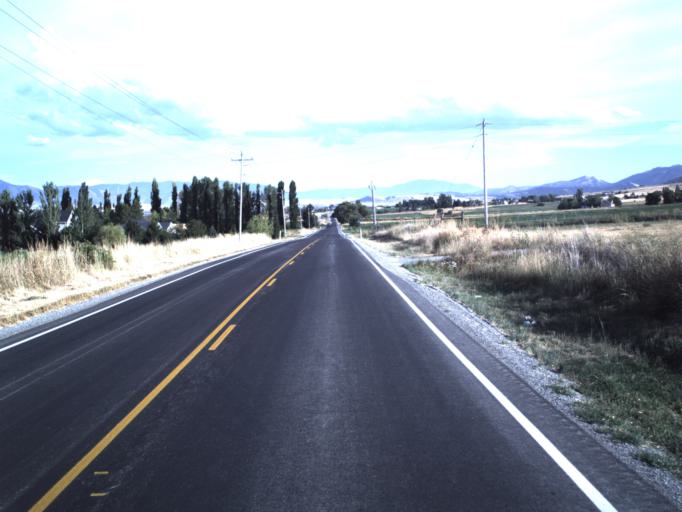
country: US
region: Utah
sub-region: Cache County
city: Mendon
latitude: 41.6870
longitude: -111.9664
